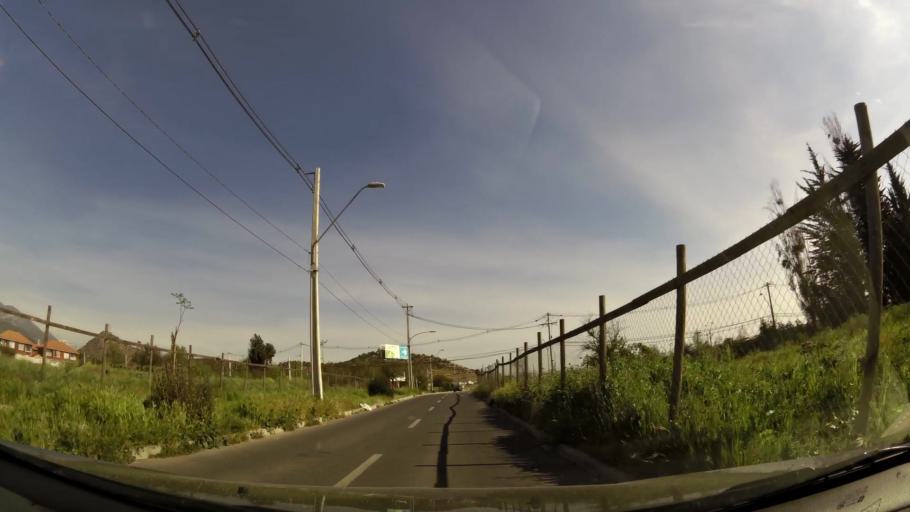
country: CL
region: Santiago Metropolitan
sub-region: Provincia de Cordillera
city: Puente Alto
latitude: -33.5923
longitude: -70.5522
